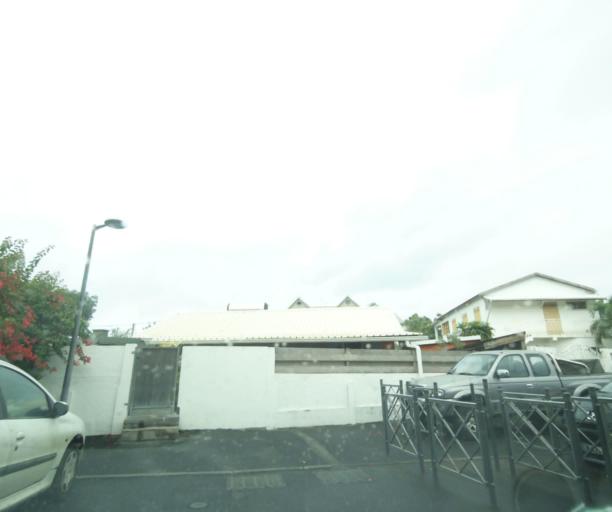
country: RE
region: Reunion
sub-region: Reunion
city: Saint-Paul
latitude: -21.0123
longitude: 55.2655
